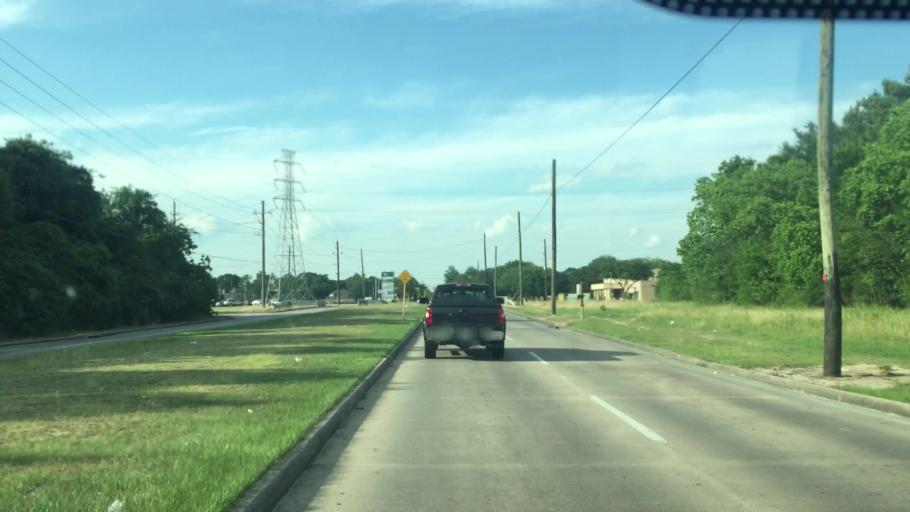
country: US
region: Texas
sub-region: Harris County
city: Hudson
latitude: 29.9702
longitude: -95.4953
